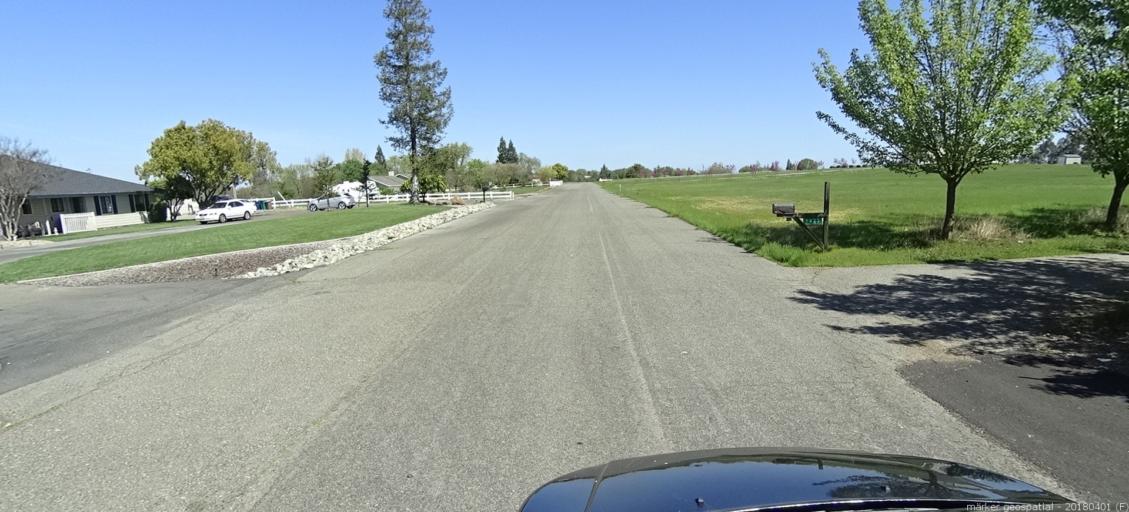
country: US
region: California
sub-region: Sacramento County
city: Wilton
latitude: 38.4123
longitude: -121.2123
